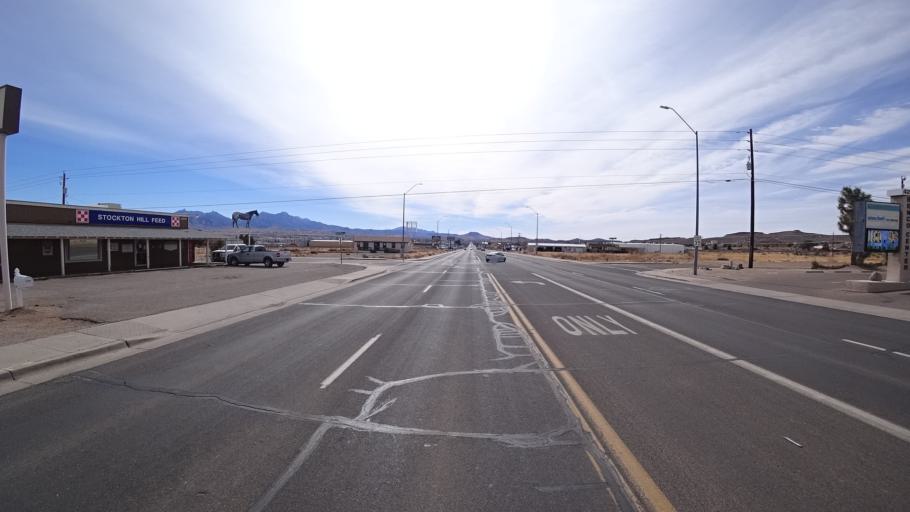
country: US
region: Arizona
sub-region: Mohave County
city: New Kingman-Butler
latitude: 35.2471
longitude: -114.0386
